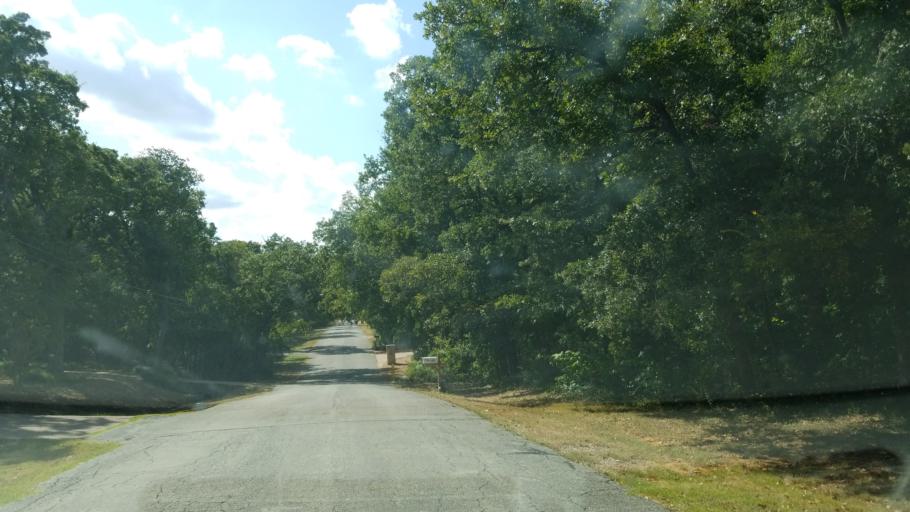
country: US
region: Texas
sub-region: Tarrant County
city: Euless
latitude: 32.8615
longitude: -97.0839
